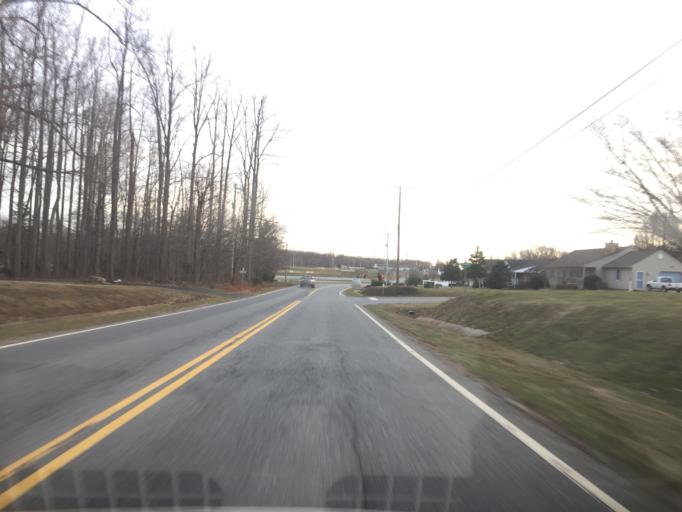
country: US
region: Virginia
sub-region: Bedford County
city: Forest
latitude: 37.3383
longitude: -79.2861
